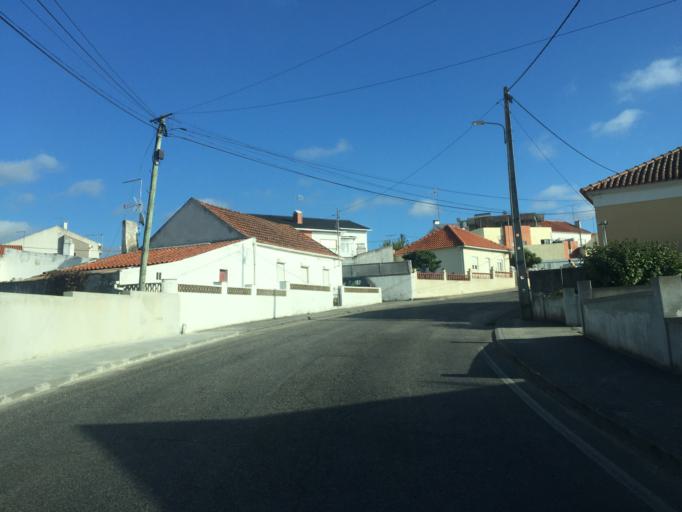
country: PT
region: Lisbon
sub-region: Torres Vedras
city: A dos Cunhados
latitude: 39.1544
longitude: -9.2983
